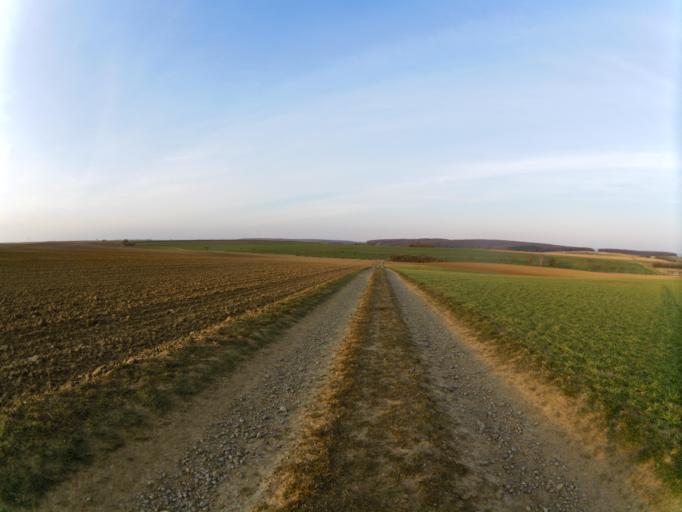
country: DE
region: Bavaria
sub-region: Regierungsbezirk Unterfranken
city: Prosselsheim
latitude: 49.8366
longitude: 10.1294
